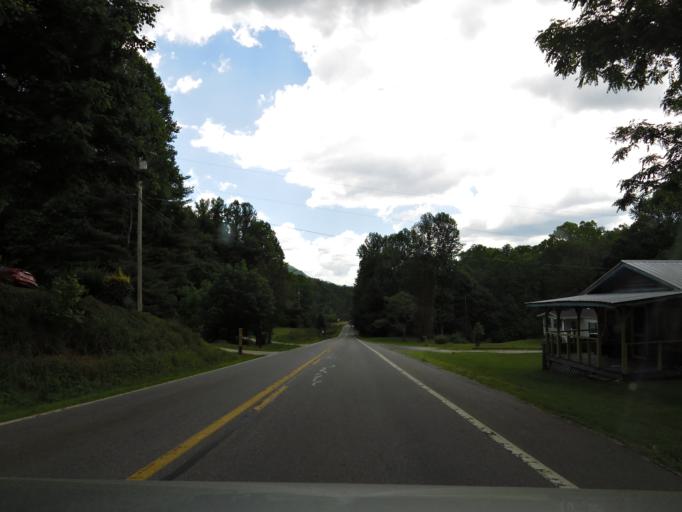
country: US
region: North Carolina
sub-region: Cherokee County
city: Andrews
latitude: 35.2383
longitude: -83.7116
